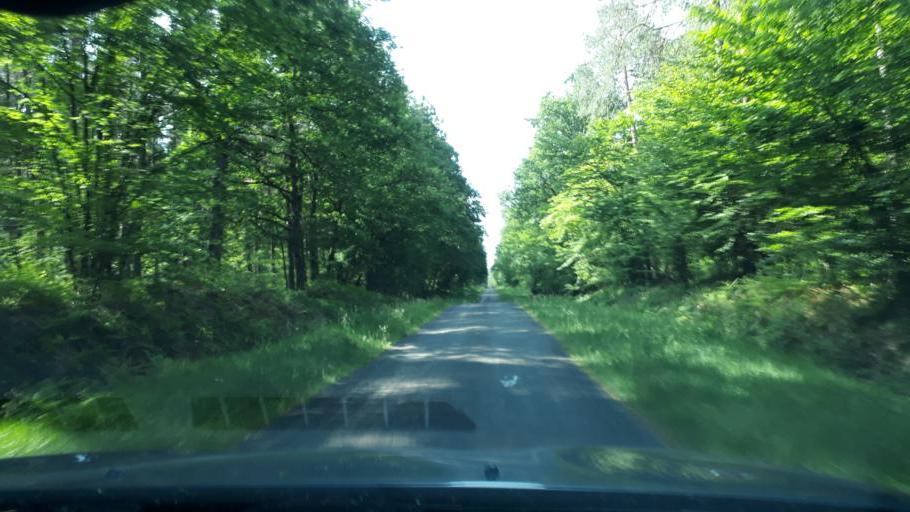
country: FR
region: Centre
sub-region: Departement du Loiret
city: Vitry-aux-Loges
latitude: 48.0303
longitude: 2.2585
